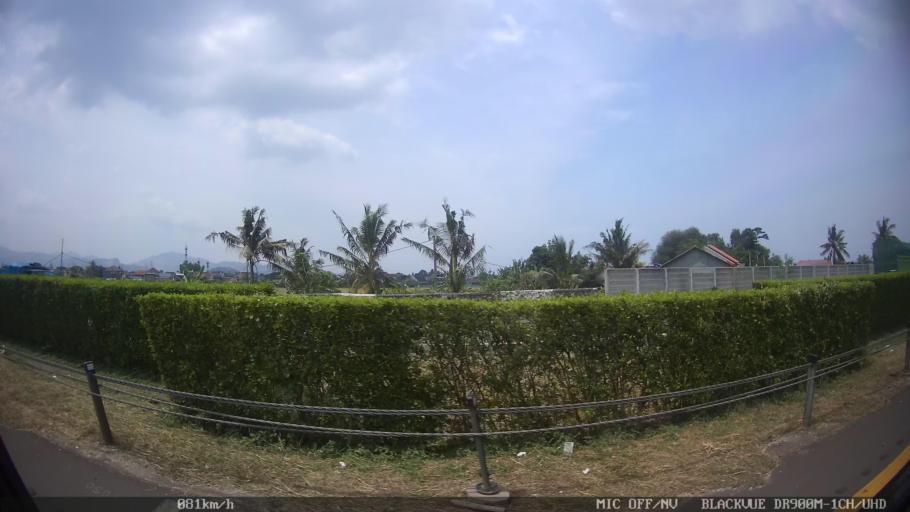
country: ID
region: Banten
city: Bojonegara
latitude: -6.0073
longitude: 106.0692
